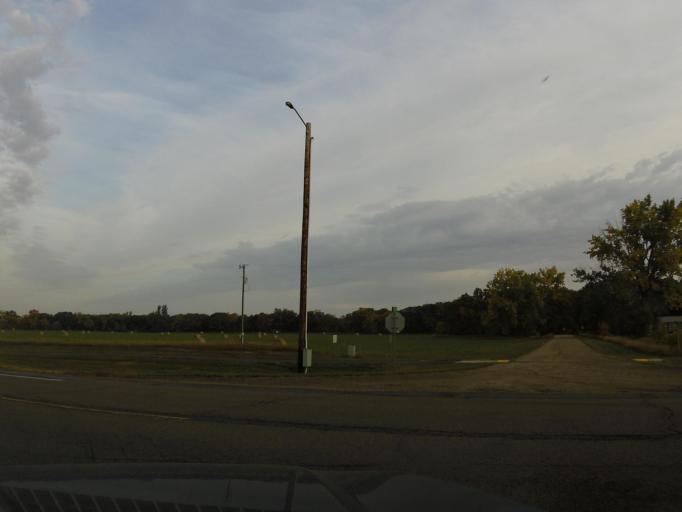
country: US
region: North Dakota
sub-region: Pembina County
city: Cavalier
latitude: 48.7733
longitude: -97.7285
